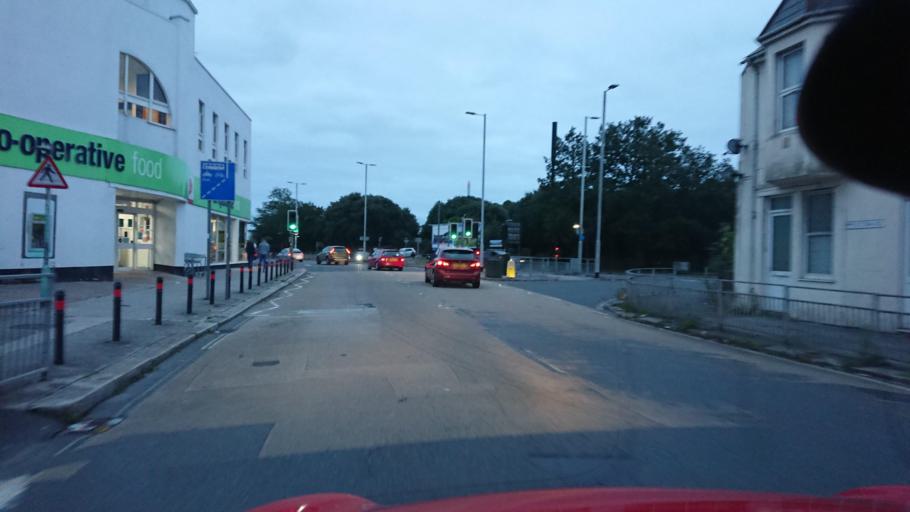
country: GB
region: England
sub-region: Cornwall
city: Torpoint
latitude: 50.4027
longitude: -4.1872
